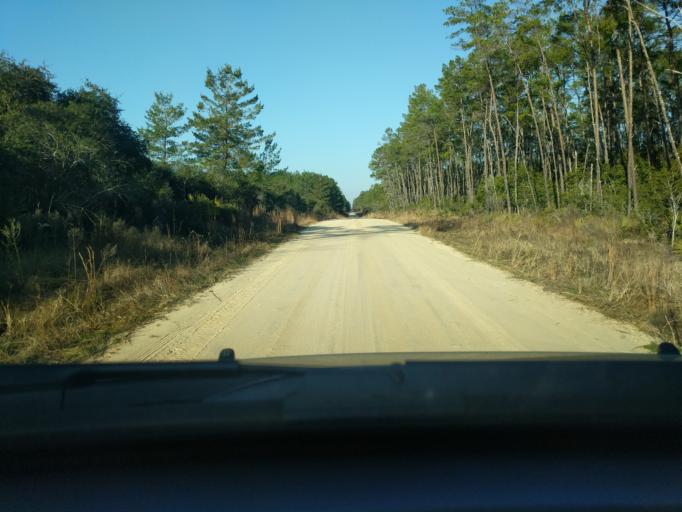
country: US
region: Florida
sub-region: Lake County
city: Astor
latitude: 29.2261
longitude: -81.7799
